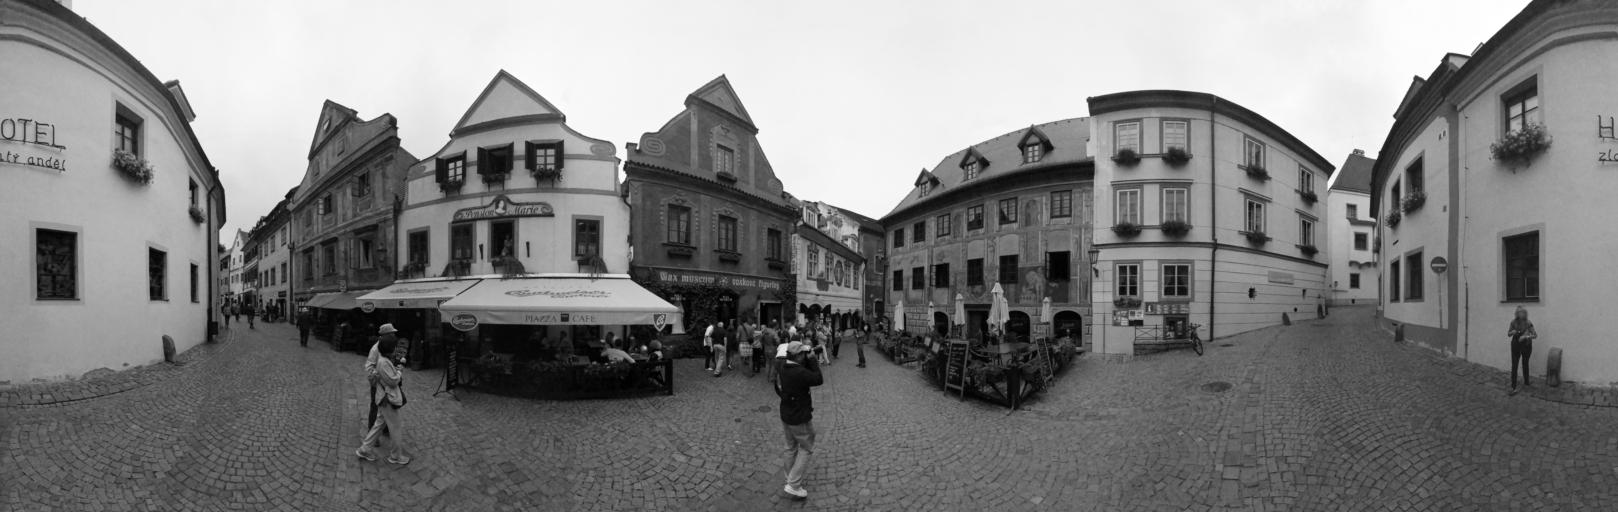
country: CZ
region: Jihocesky
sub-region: Okres Cesky Krumlov
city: Cesky Krumlov
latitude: 48.8104
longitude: 14.3140
